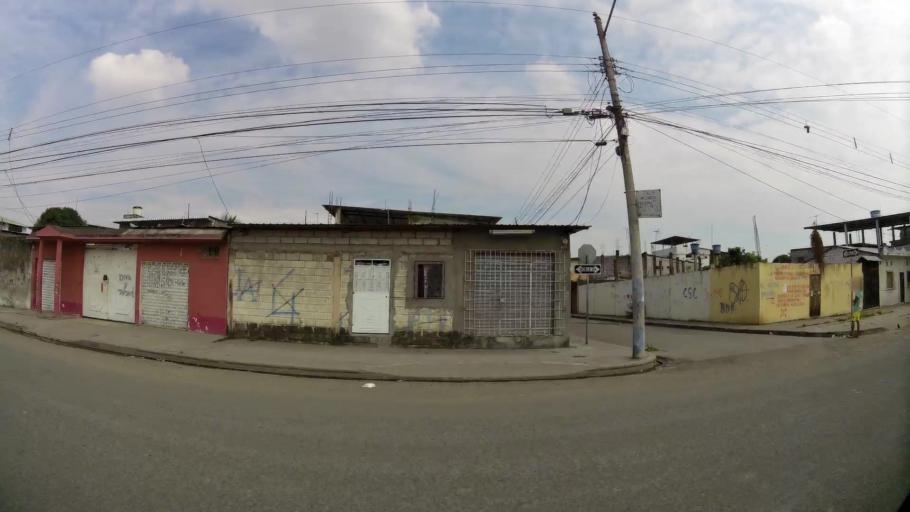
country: EC
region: Guayas
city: Guayaquil
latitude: -2.2411
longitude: -79.9088
